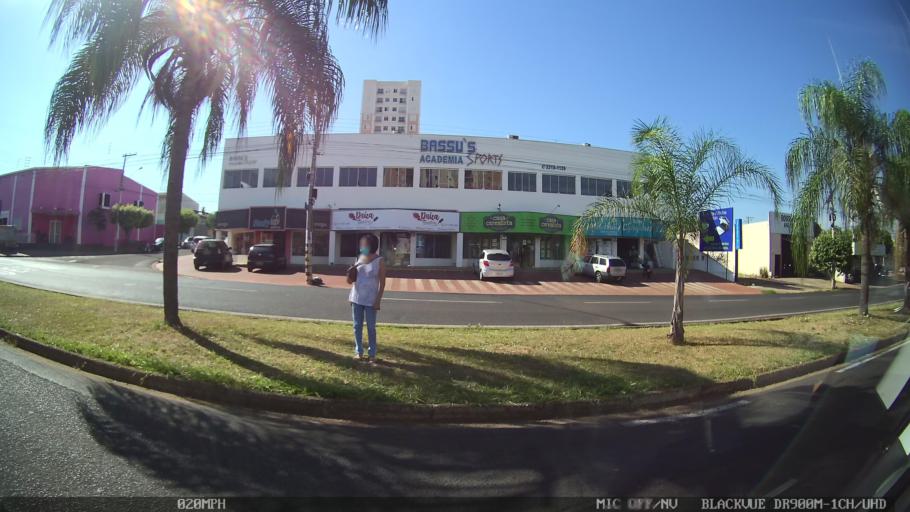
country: BR
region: Sao Paulo
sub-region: Sao Jose Do Rio Preto
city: Sao Jose do Rio Preto
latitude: -20.7858
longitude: -49.3686
